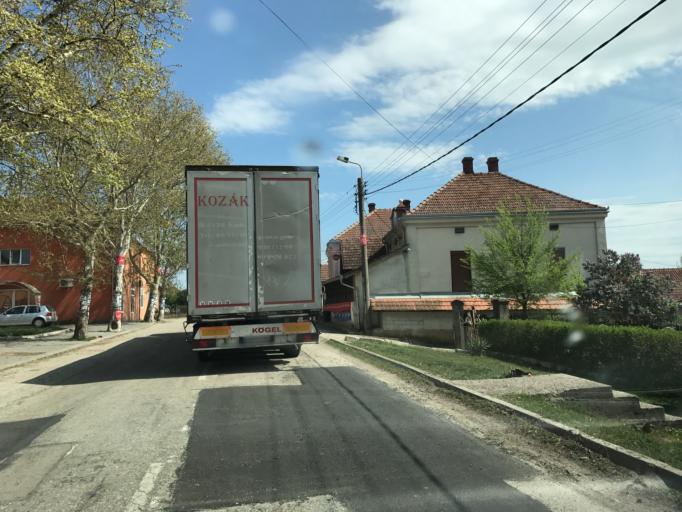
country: RS
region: Central Serbia
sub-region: Zajecarski Okrug
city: Zajecar
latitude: 43.9017
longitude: 22.2143
